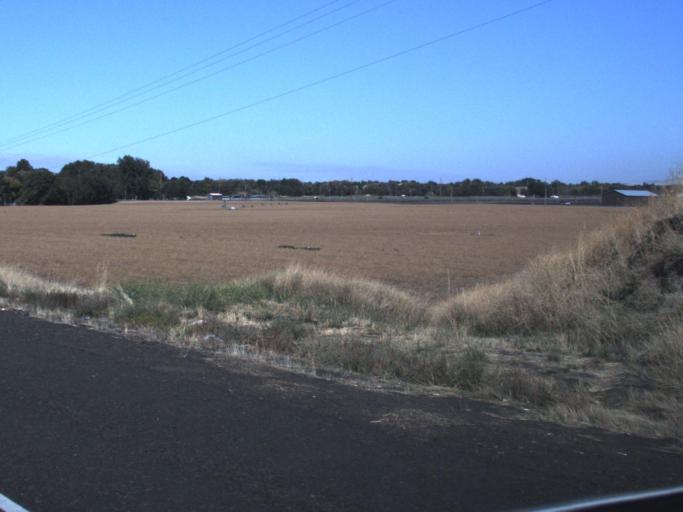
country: US
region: Washington
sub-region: Walla Walla County
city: College Place
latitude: 46.0182
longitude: -118.3890
